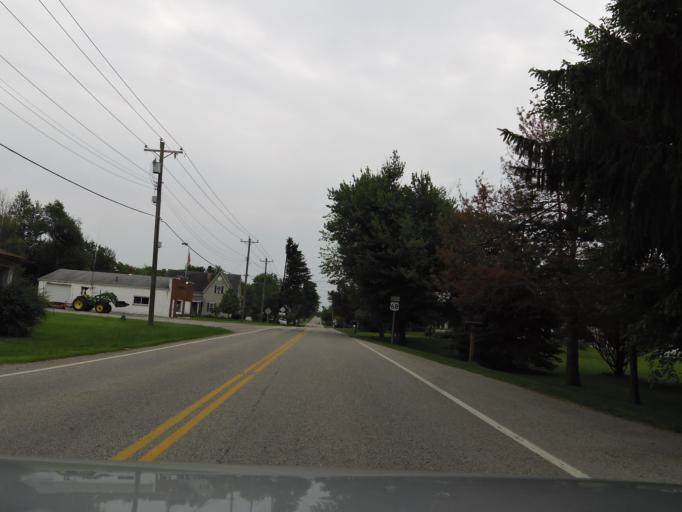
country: US
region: Ohio
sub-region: Clinton County
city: Blanchester
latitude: 39.2807
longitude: -83.9107
